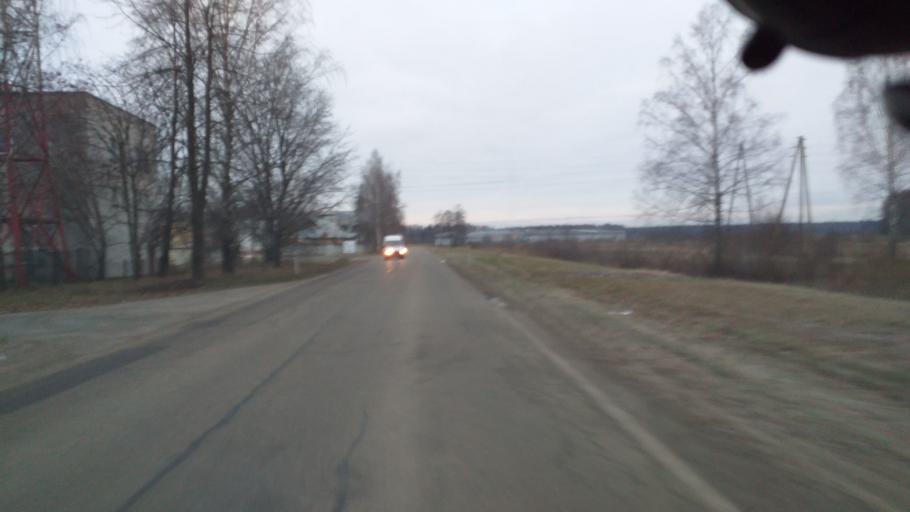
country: LV
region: Olaine
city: Olaine
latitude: 56.7981
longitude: 23.9345
